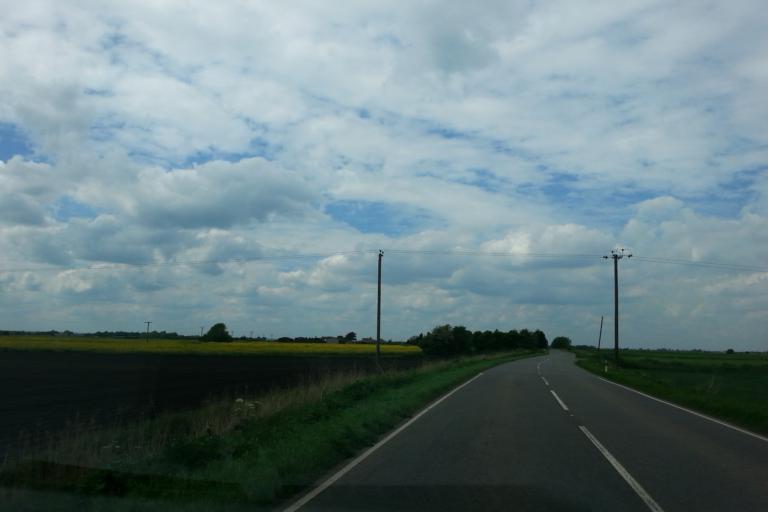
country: GB
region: England
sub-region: Cambridgeshire
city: Ramsey
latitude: 52.4633
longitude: -0.1247
